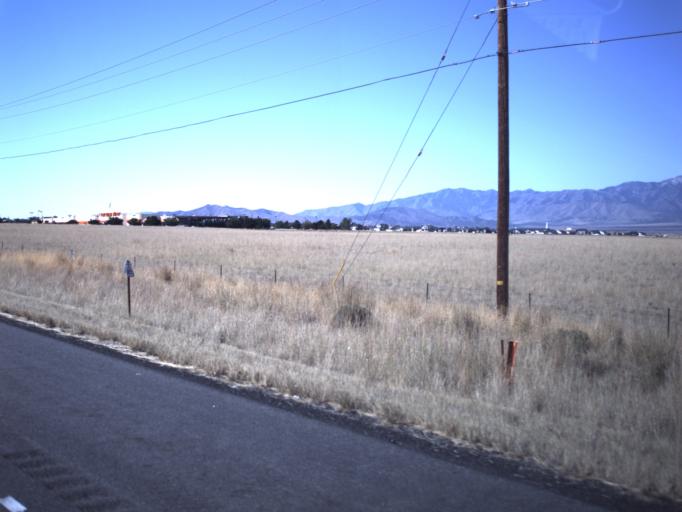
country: US
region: Utah
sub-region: Tooele County
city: Erda
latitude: 40.5762
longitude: -112.2946
